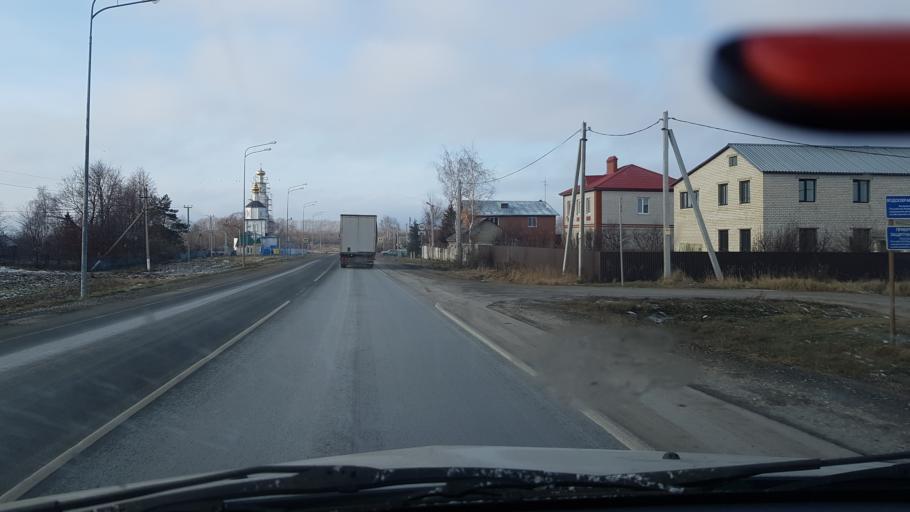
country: RU
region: Tatarstan
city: Laishevo
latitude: 55.3919
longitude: 49.8046
